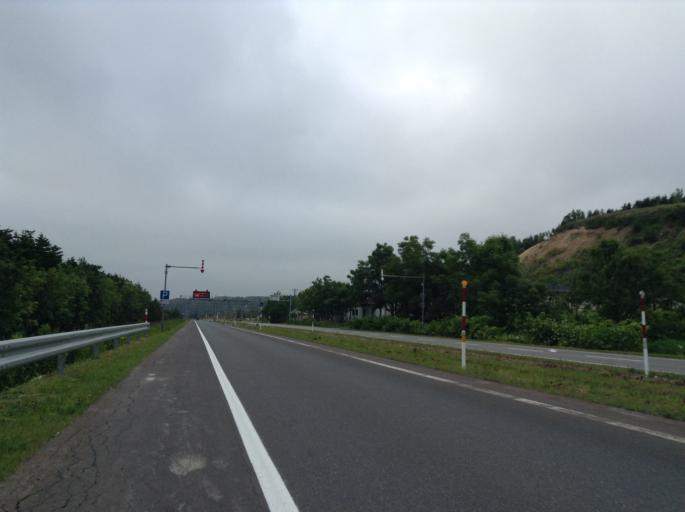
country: JP
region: Hokkaido
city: Wakkanai
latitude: 45.3663
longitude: 141.7284
